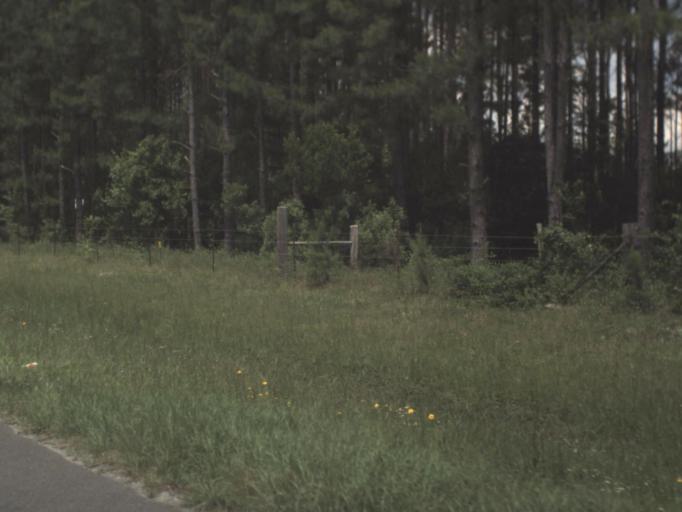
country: US
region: Florida
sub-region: Columbia County
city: Five Points
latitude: 30.2877
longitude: -82.6306
